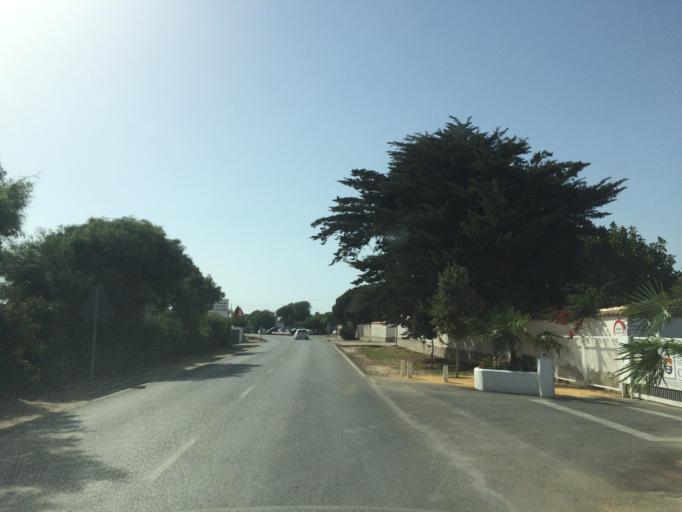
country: ES
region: Andalusia
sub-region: Provincia de Cadiz
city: Vejer de la Frontera
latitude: 36.1899
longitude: -6.0257
